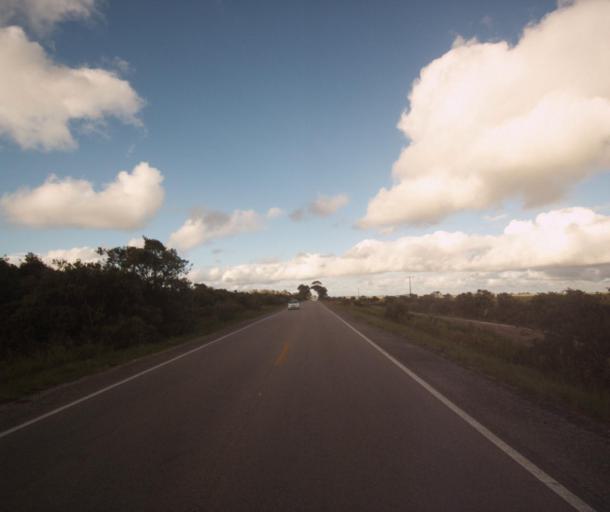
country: BR
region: Rio Grande do Sul
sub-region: Rio Grande
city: Rio Grande
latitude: -32.1909
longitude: -52.4338
